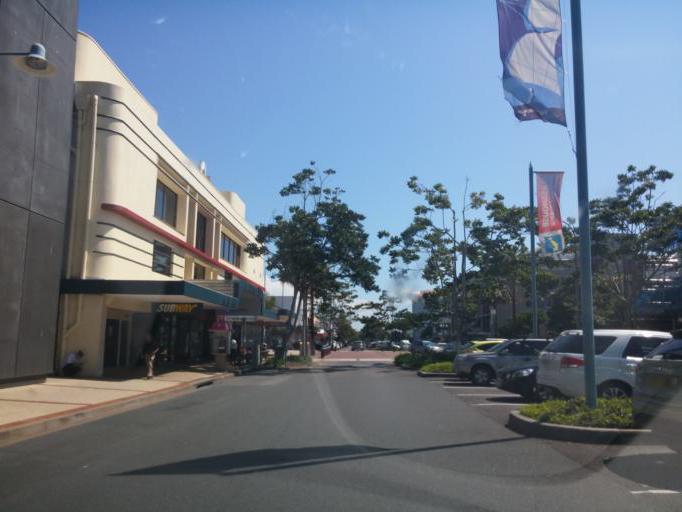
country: AU
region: New South Wales
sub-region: Port Macquarie-Hastings
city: Port Macquarie
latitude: -31.4291
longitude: 152.9091
